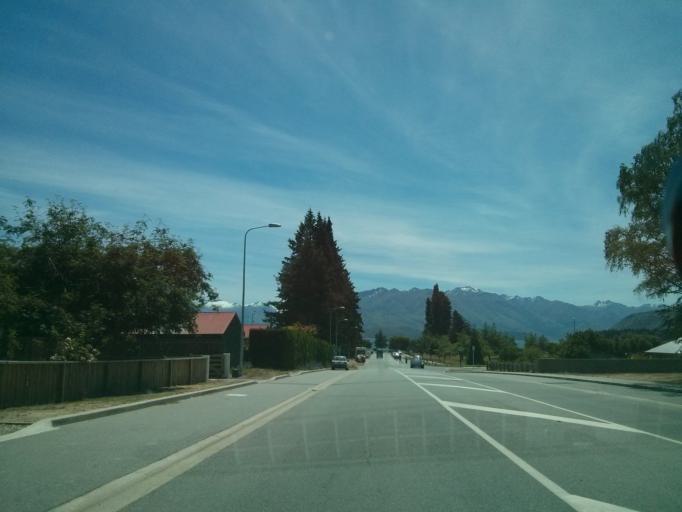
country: NZ
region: Otago
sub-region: Queenstown-Lakes District
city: Wanaka
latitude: -44.7013
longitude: 169.1300
